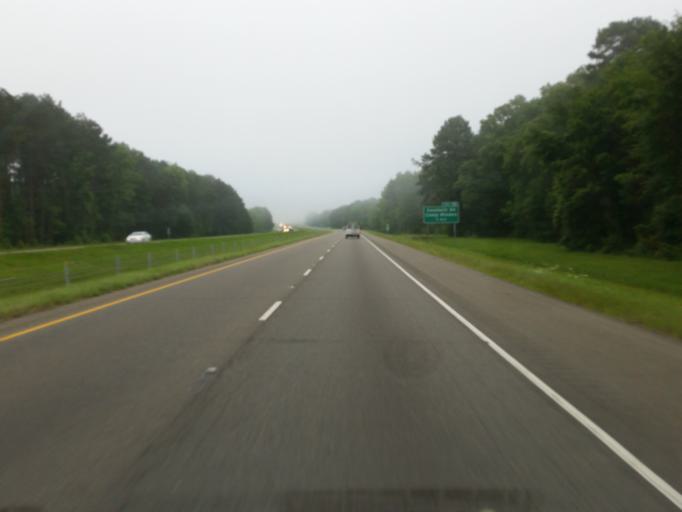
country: US
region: Louisiana
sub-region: Bossier Parish
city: Haughton
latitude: 32.5770
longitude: -93.4545
